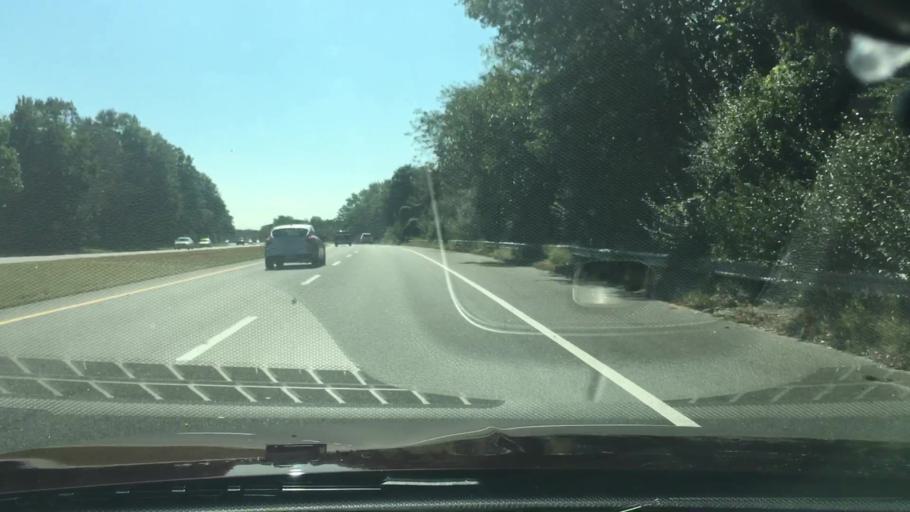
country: US
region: New York
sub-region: Suffolk County
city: North Bellport
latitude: 40.8015
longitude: -72.9591
